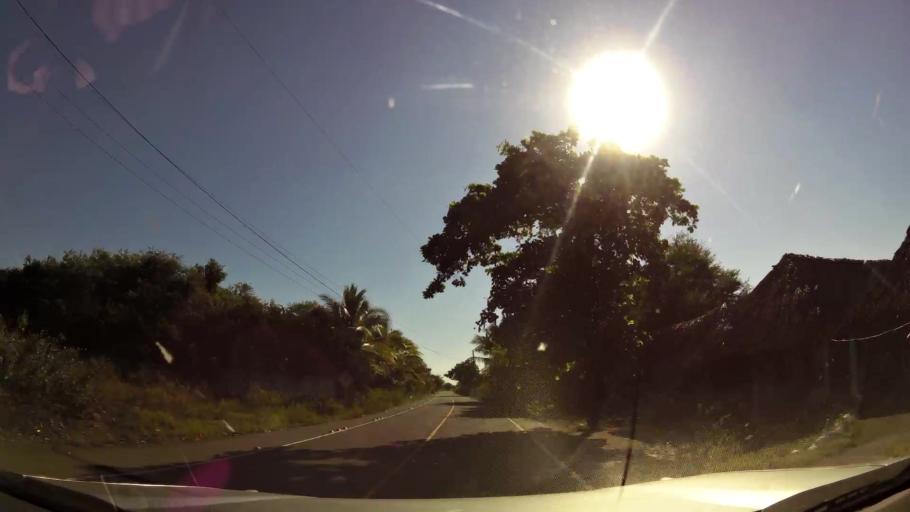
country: GT
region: Santa Rosa
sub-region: Municipio de Taxisco
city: Taxisco
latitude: 13.8840
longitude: -90.4590
